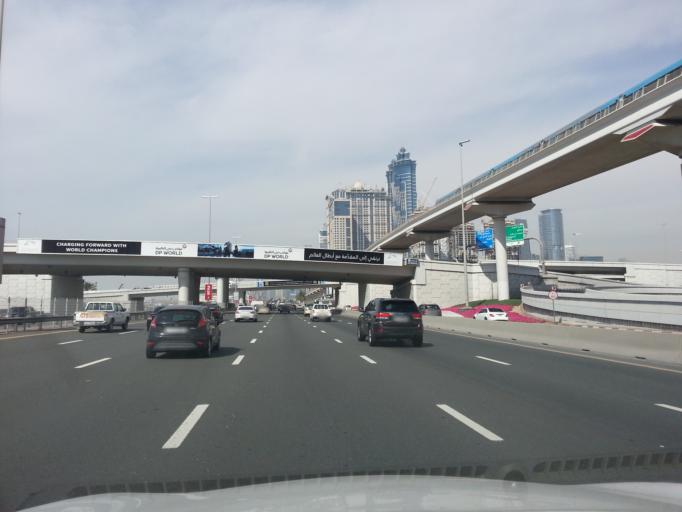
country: AE
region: Dubai
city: Dubai
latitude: 25.1791
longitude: 55.2487
